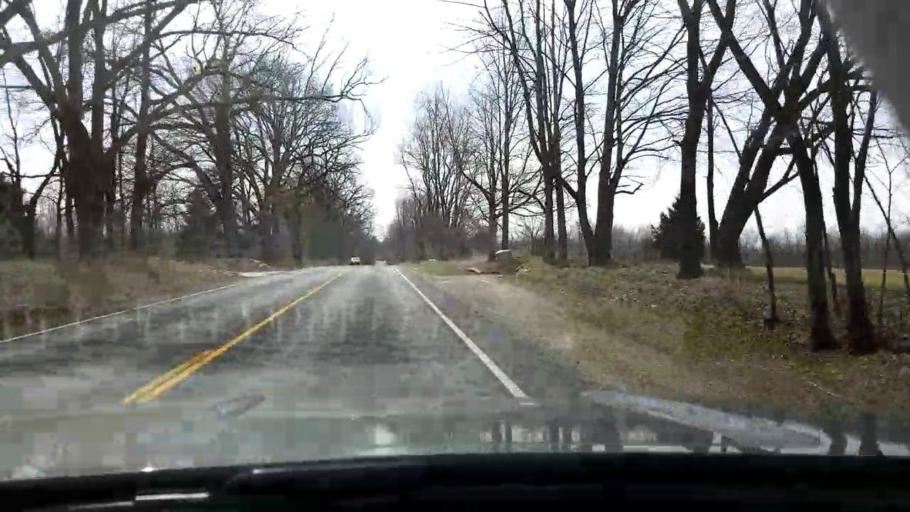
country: US
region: Michigan
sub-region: Jackson County
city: Spring Arbor
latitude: 42.1831
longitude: -84.5204
